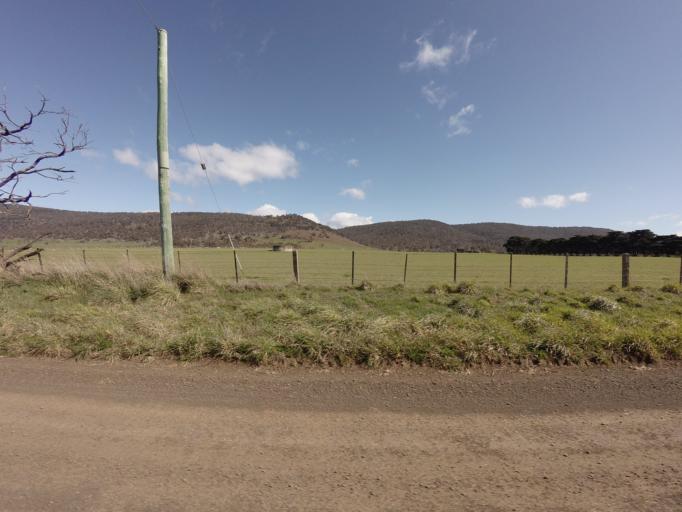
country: AU
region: Tasmania
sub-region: Northern Midlands
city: Evandale
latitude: -41.9516
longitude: 147.4352
